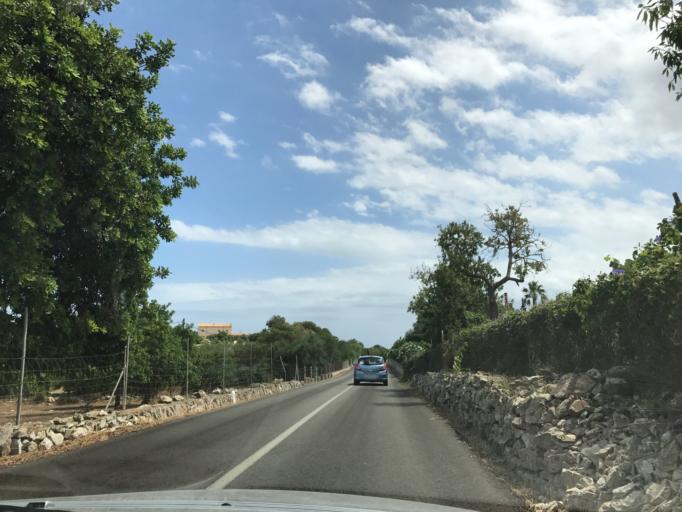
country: ES
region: Balearic Islands
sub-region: Illes Balears
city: Son Servera
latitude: 39.6385
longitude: 3.3513
